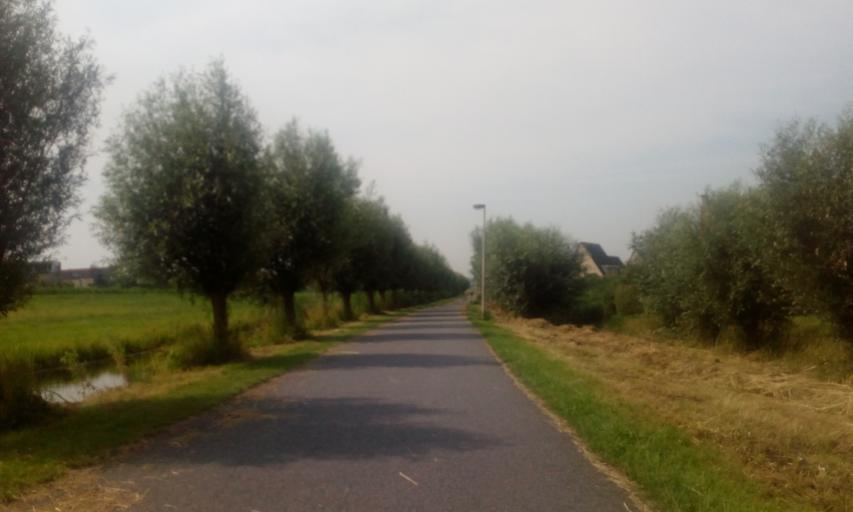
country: NL
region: South Holland
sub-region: Gemeente Krimpen aan den IJssel
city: Krimpen aan den IJssel
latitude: 51.9587
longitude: 4.6144
